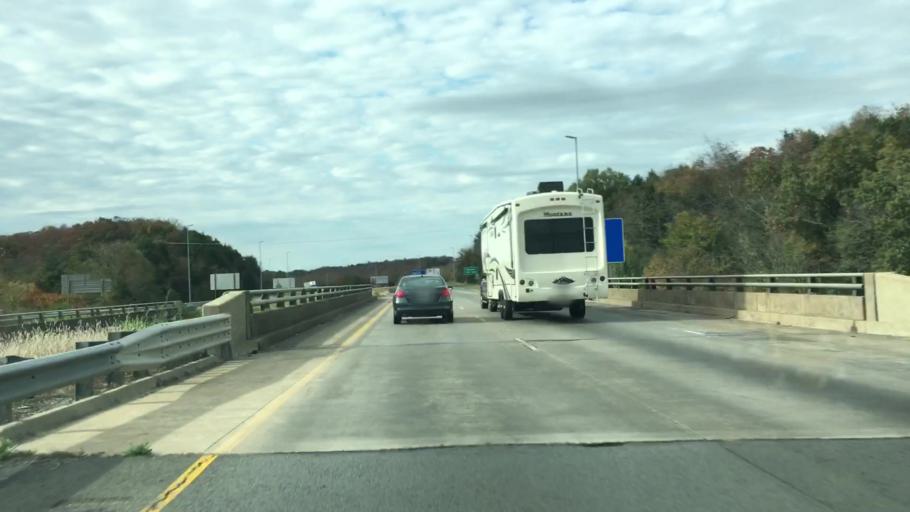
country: US
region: Arkansas
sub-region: Faulkner County
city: Conway
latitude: 35.1157
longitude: -92.4478
